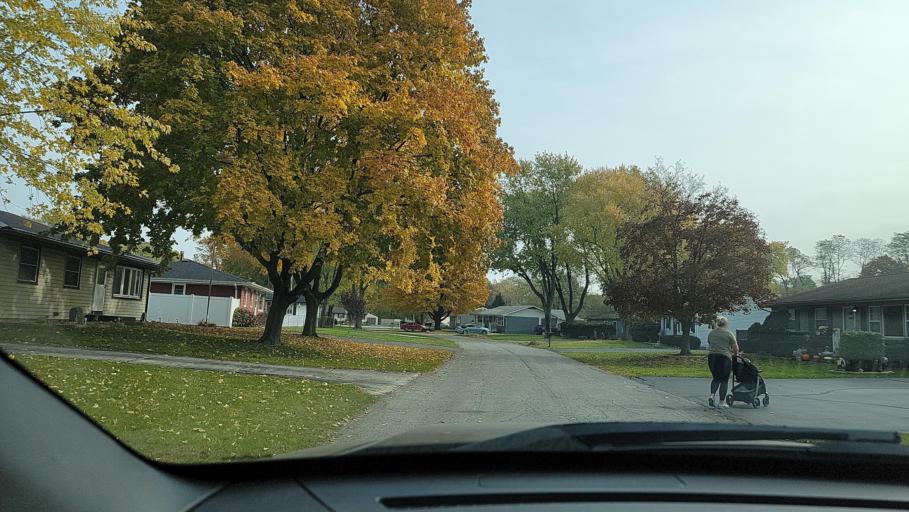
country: US
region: Indiana
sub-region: Porter County
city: Portage
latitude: 41.5895
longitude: -87.1812
